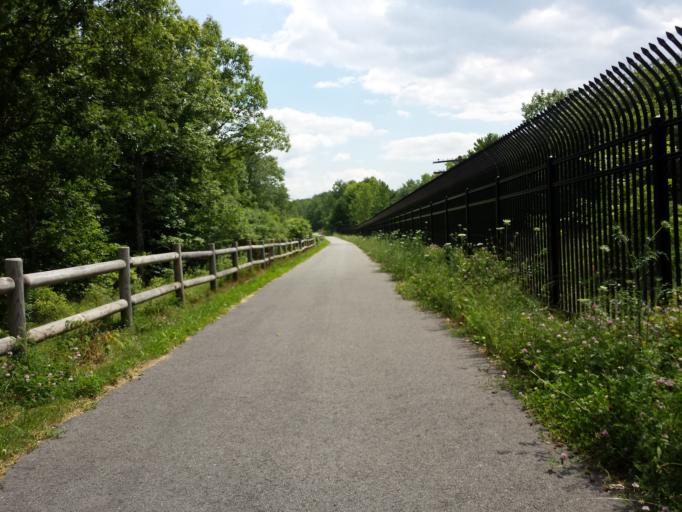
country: US
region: New York
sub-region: Saratoga County
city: Ballston Spa
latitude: 42.9952
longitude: -73.8404
